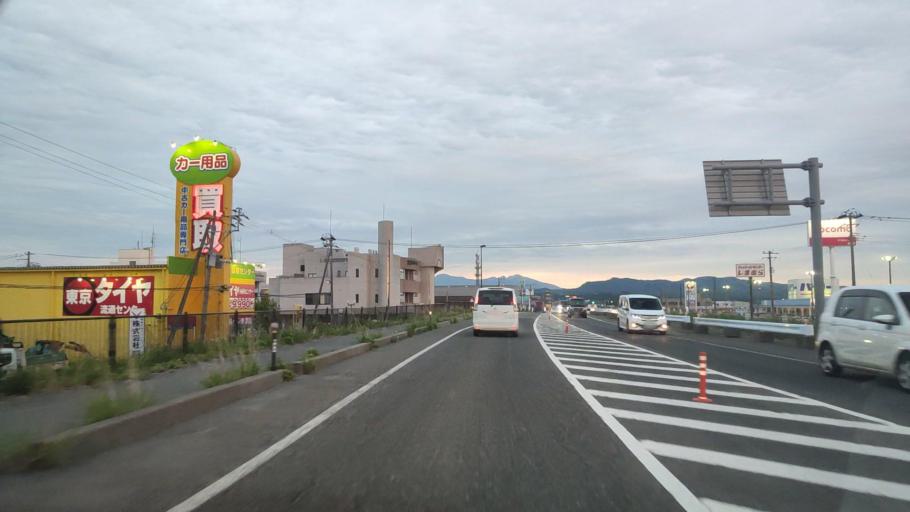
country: JP
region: Niigata
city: Niitsu-honcho
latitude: 37.7923
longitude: 139.1108
